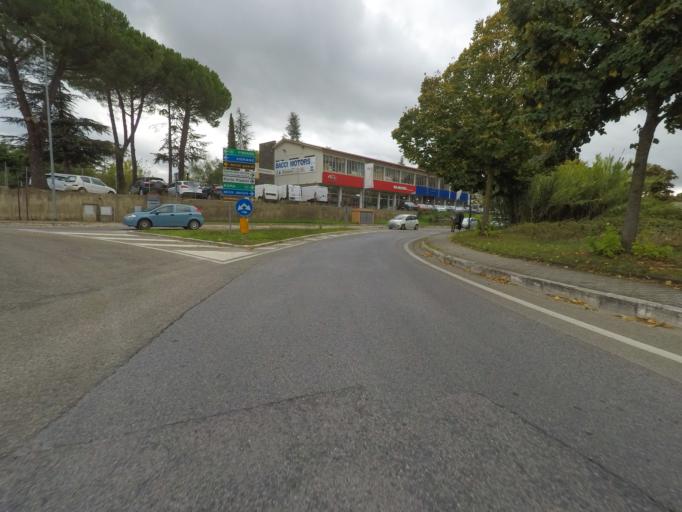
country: IT
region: Tuscany
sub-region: Provincia di Siena
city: Siena
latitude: 43.3210
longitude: 11.3501
